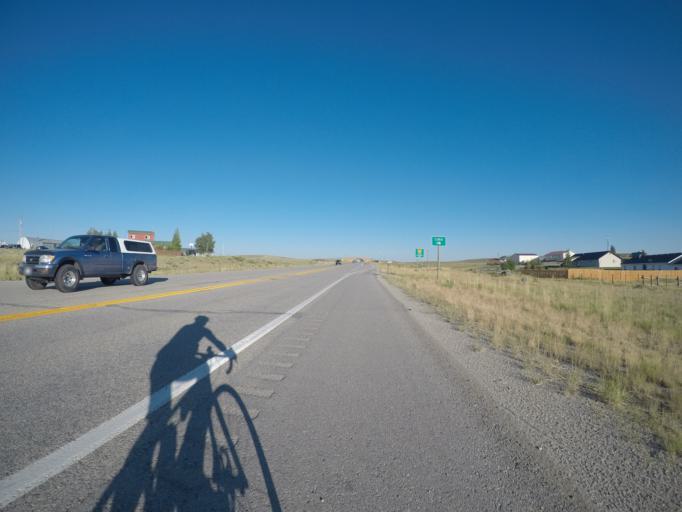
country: US
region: Wyoming
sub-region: Sublette County
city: Pinedale
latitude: 42.8803
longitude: -109.9718
